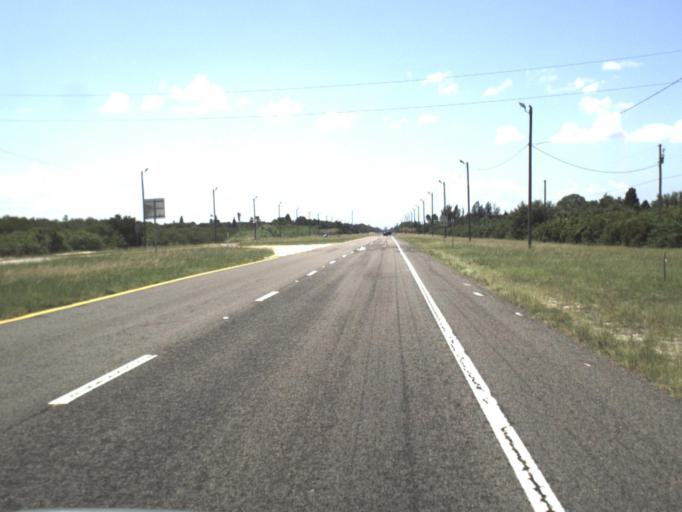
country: US
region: Florida
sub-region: Pinellas County
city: Feather Sound
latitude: 27.8881
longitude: -82.6390
